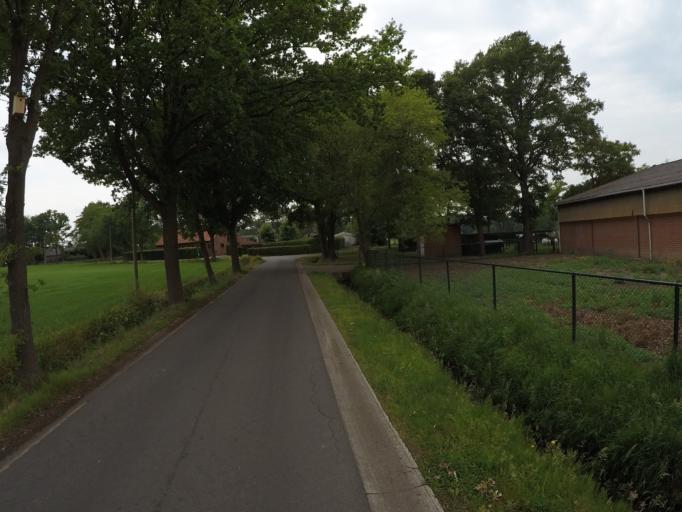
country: BE
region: Flanders
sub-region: Provincie Antwerpen
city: Wuustwezel
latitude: 51.4122
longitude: 4.5891
